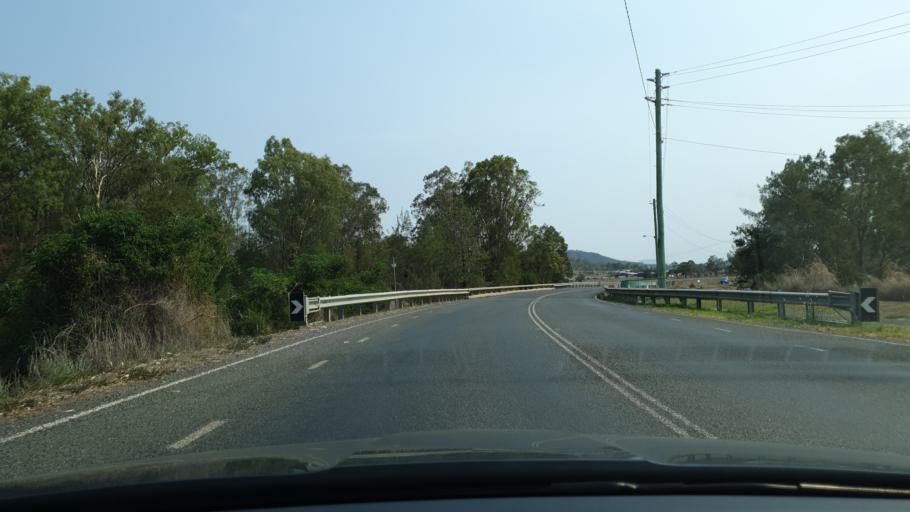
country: AU
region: Queensland
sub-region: Ipswich
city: Deebing Heights
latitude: -28.0071
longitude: 152.6804
